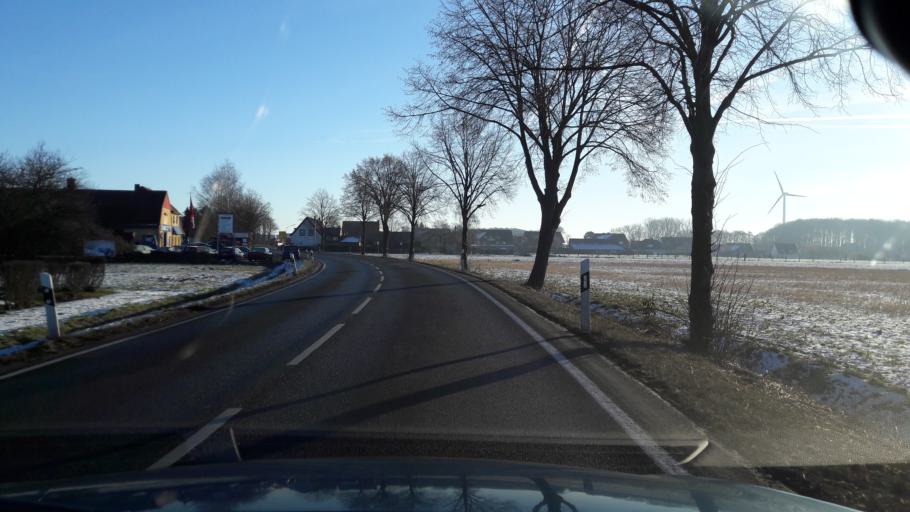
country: DE
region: North Rhine-Westphalia
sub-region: Regierungsbezirk Munster
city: Wadersloh
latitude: 51.7337
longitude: 8.1675
